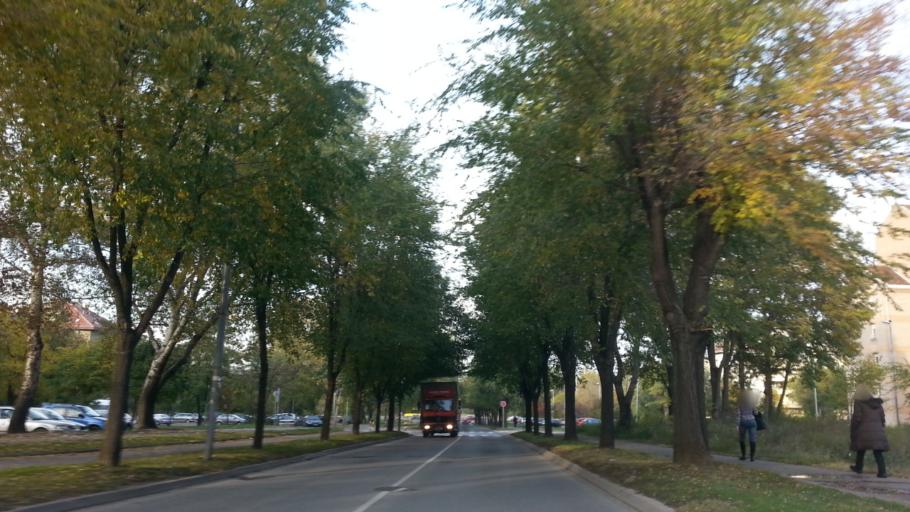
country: RS
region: Central Serbia
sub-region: Belgrade
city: Zemun
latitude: 44.8183
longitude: 20.3774
